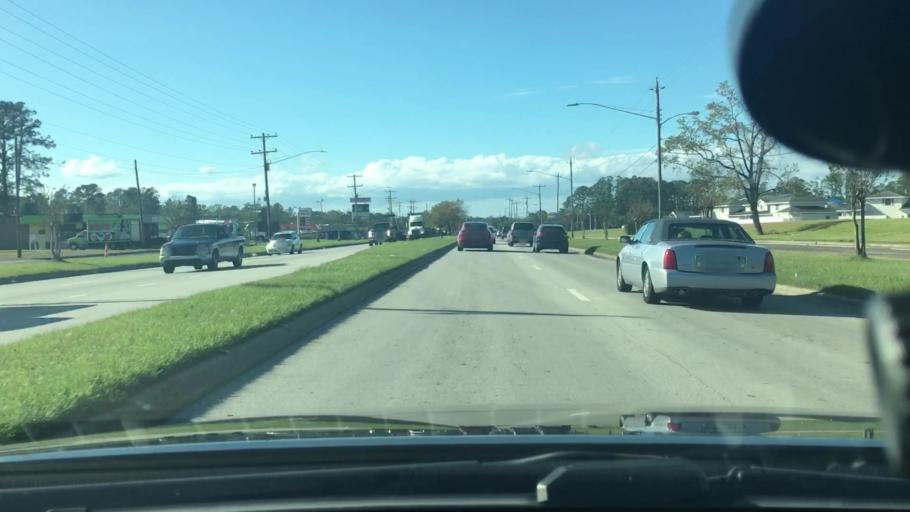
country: US
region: North Carolina
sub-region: Craven County
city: Havelock
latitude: 34.8847
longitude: -76.9131
